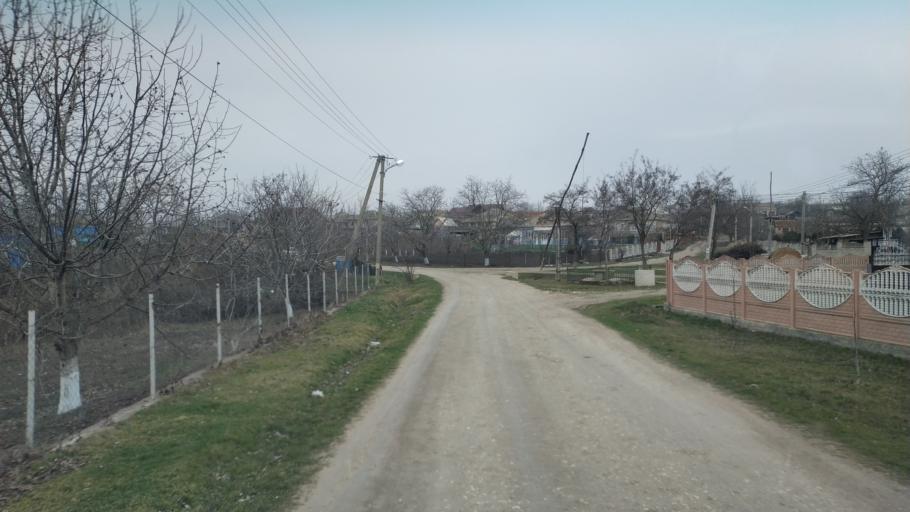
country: MD
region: Chisinau
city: Singera
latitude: 46.8253
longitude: 29.0257
